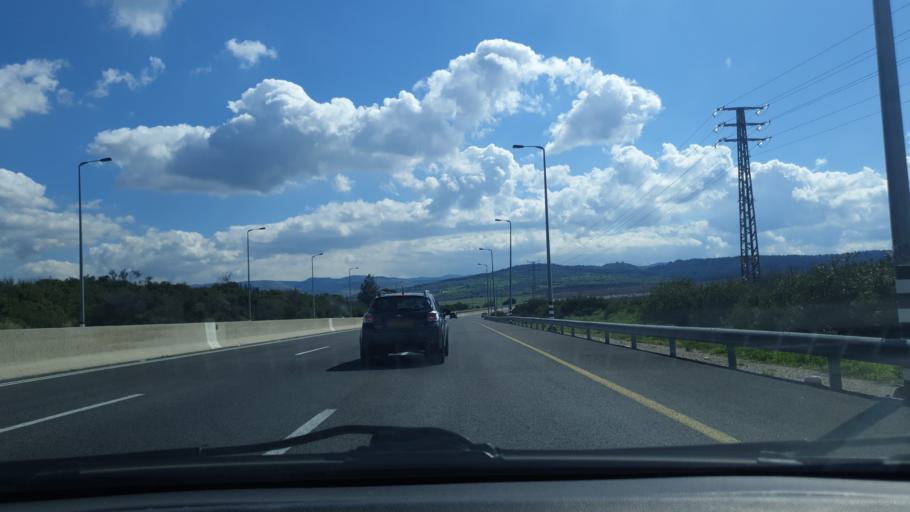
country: IL
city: Nof Ayalon
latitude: 31.8654
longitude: 34.9742
